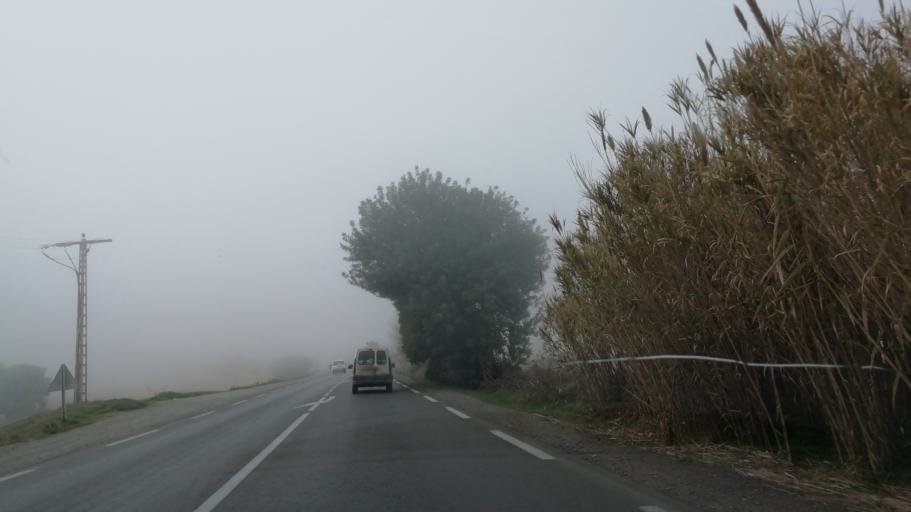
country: DZ
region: Mascara
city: Mascara
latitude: 35.5213
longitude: 0.3162
